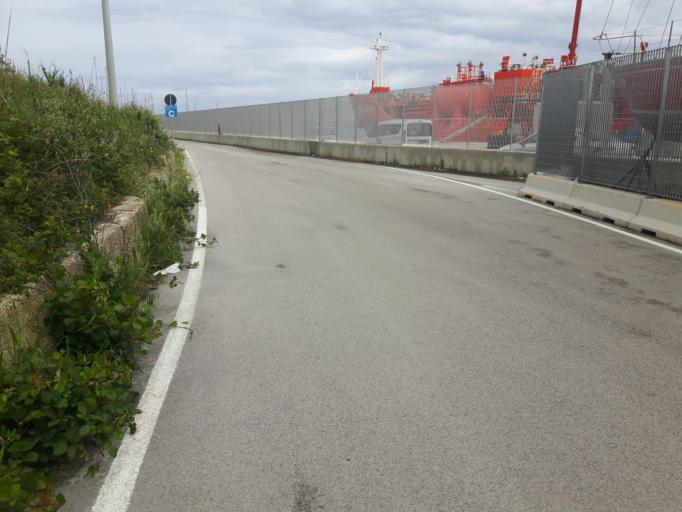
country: IT
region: Abruzzo
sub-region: Provincia di Chieti
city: Vasto
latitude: 42.1722
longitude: 14.7099
